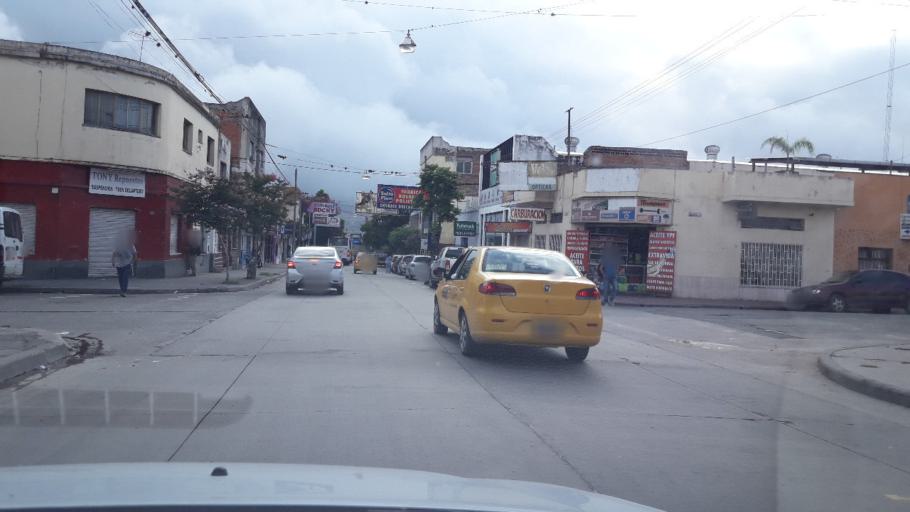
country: AR
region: Jujuy
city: San Salvador de Jujuy
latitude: -24.1911
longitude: -65.3014
